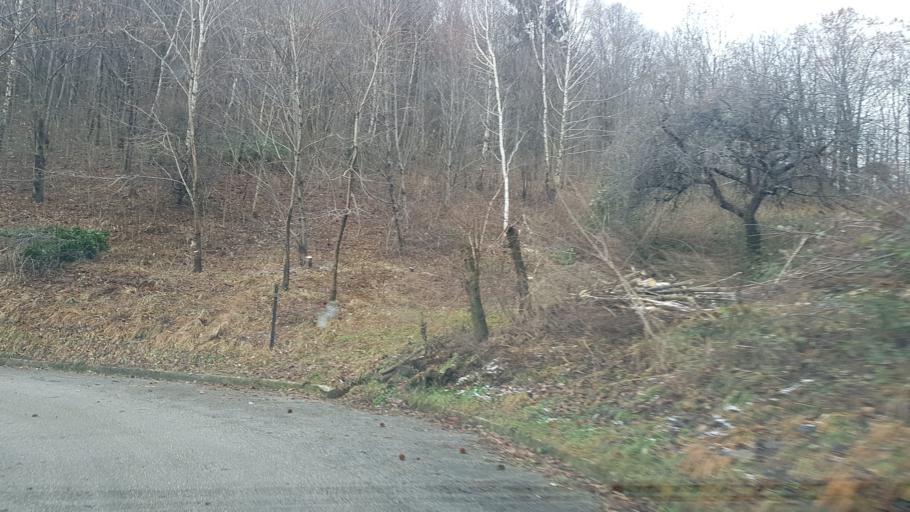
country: IT
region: Friuli Venezia Giulia
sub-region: Provincia di Udine
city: Savogna
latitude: 46.1737
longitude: 13.5518
